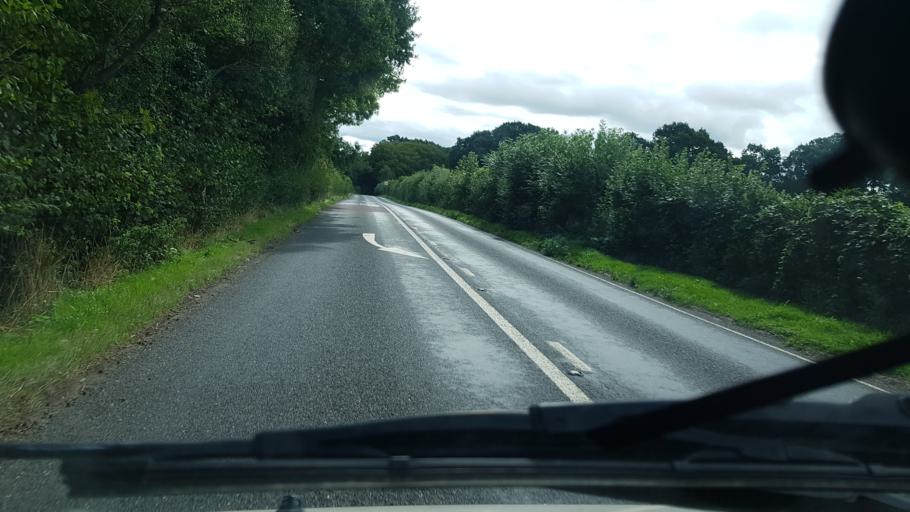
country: GB
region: England
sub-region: West Sussex
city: Rudgwick
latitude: 51.0883
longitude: -0.4664
